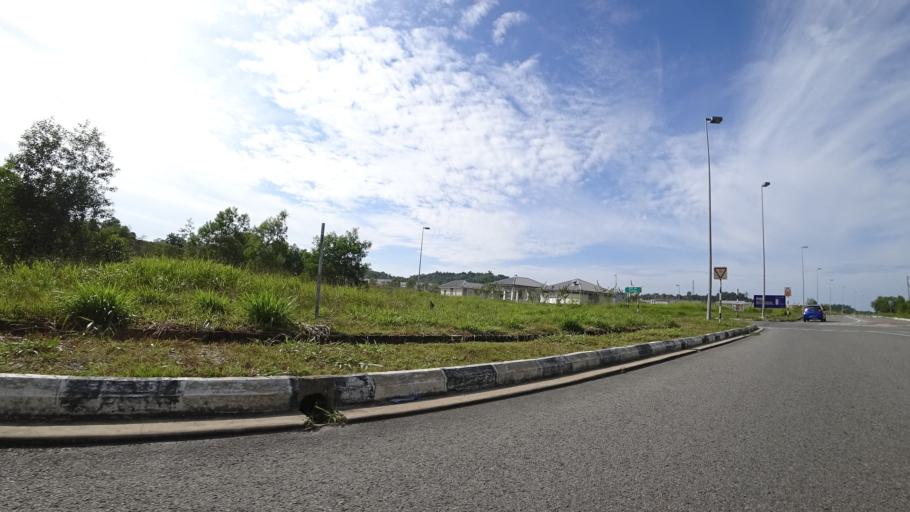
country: BN
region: Brunei and Muara
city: Bandar Seri Begawan
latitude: 4.8872
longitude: 114.8030
